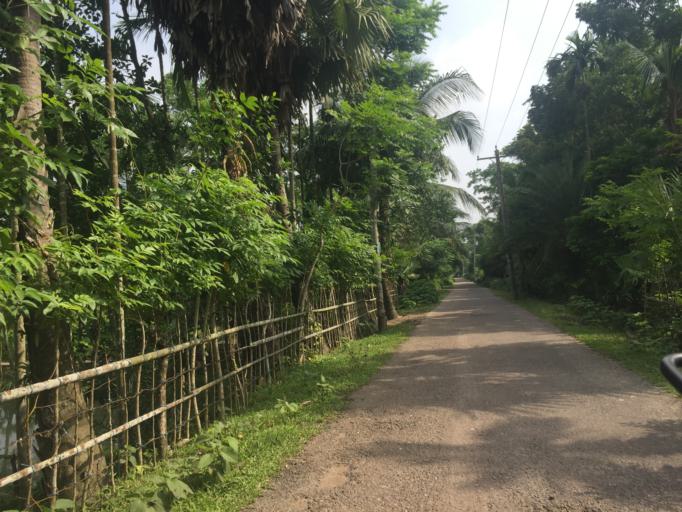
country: BD
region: Barisal
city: Mathba
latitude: 22.2210
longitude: 89.9161
